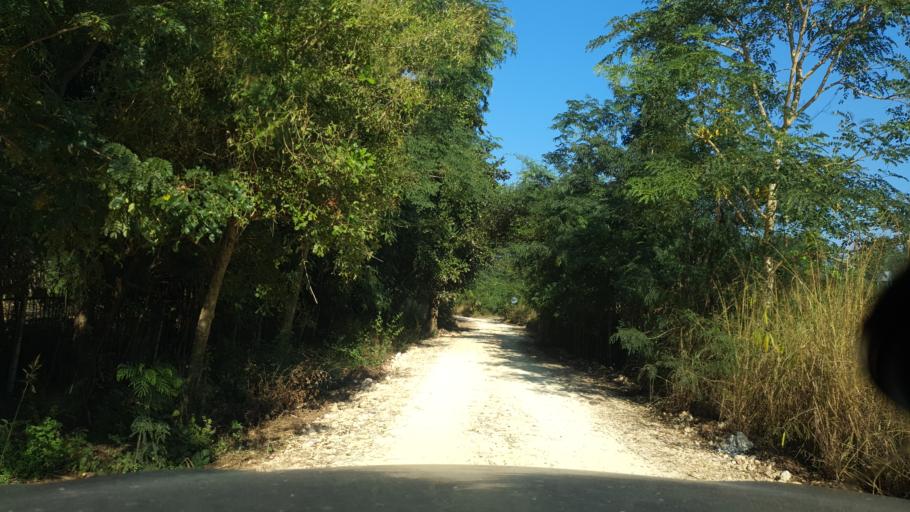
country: TH
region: Chiang Mai
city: San Kamphaeng
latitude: 18.7084
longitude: 99.0859
